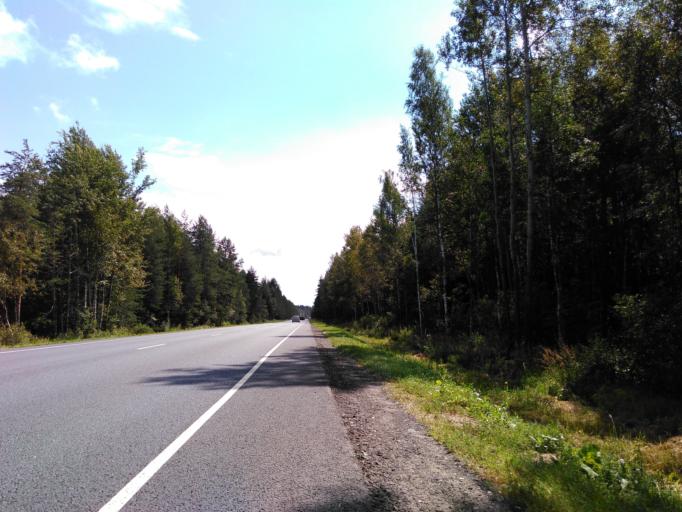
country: RU
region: Moskovskaya
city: Elektrogorsk
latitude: 56.0318
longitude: 38.7508
